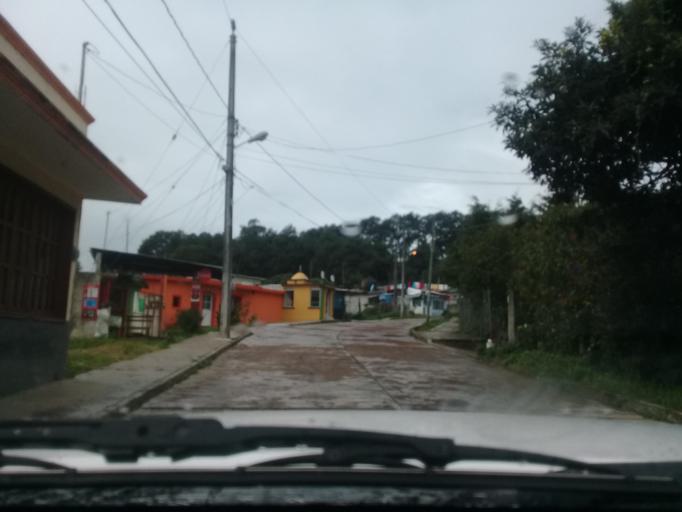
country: MX
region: Veracruz
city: Rafael Lucio
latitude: 19.5900
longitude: -96.9918
